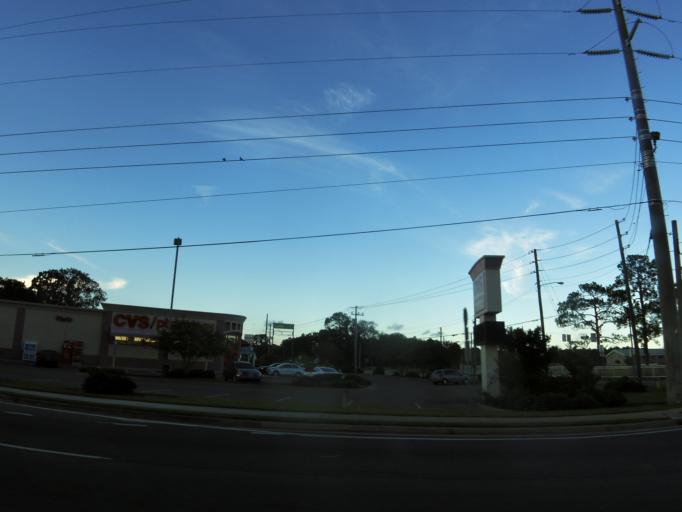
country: US
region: Georgia
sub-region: Camden County
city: St Marys
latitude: 30.7521
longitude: -81.5767
